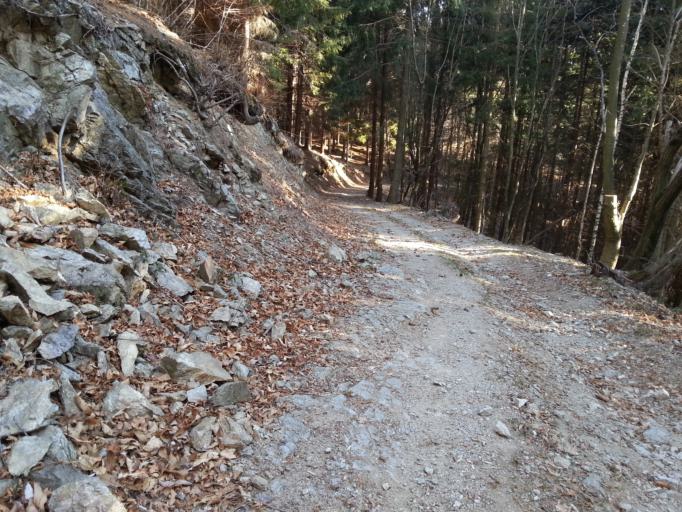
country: CH
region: Ticino
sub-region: Lugano District
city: Gravesano
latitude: 46.0439
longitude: 8.8628
